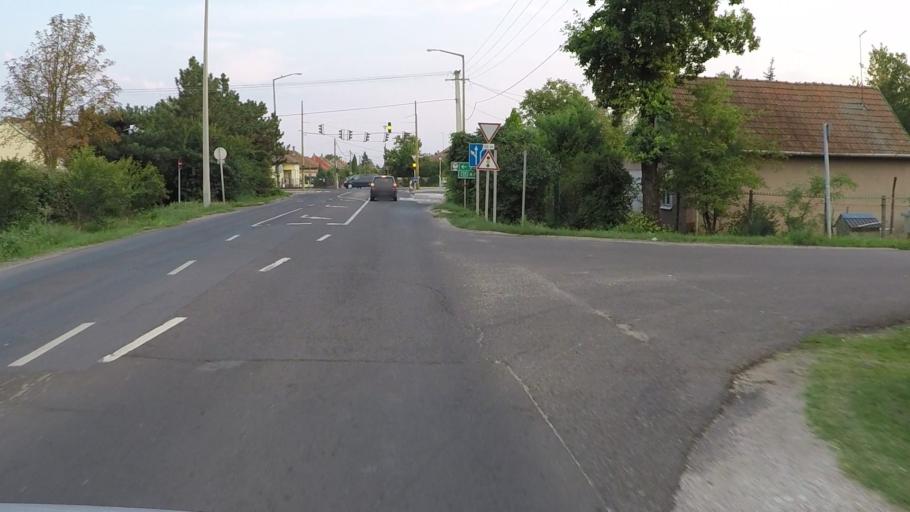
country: HU
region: Jasz-Nagykun-Szolnok
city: Szolnok
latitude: 47.1781
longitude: 20.1538
